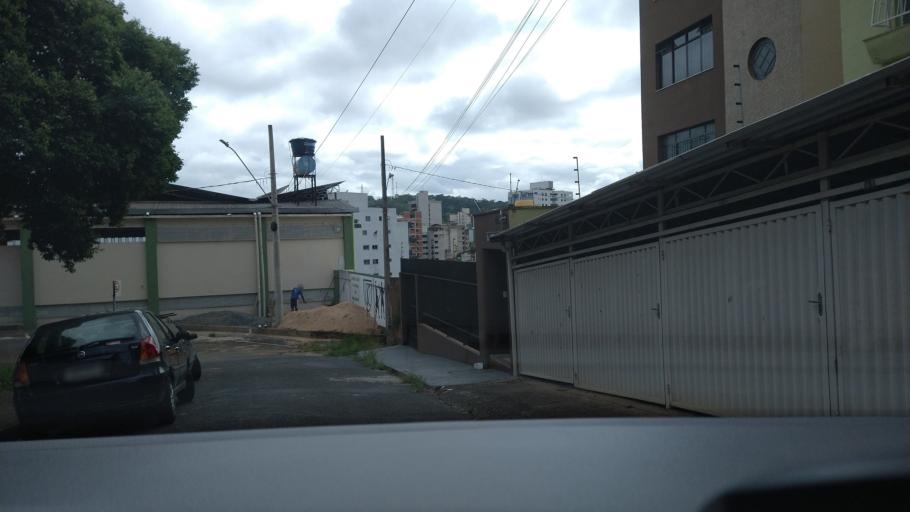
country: BR
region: Minas Gerais
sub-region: Vicosa
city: Vicosa
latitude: -20.7588
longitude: -42.8815
